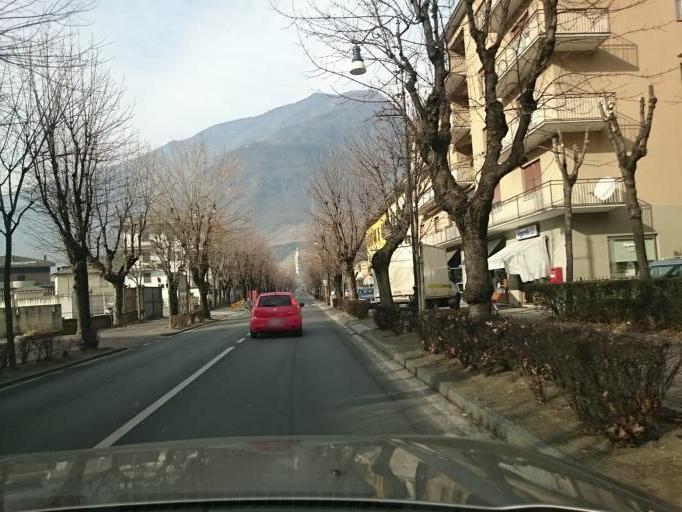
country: IT
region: Lombardy
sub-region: Provincia di Sondrio
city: Tirano
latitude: 46.2169
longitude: 10.1649
